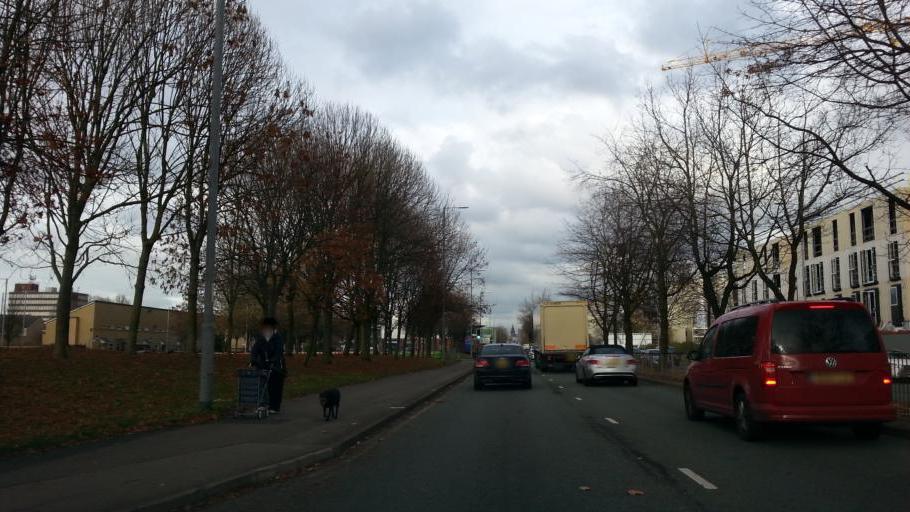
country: GB
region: England
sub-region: Manchester
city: Hulme
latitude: 53.4570
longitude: -2.2452
